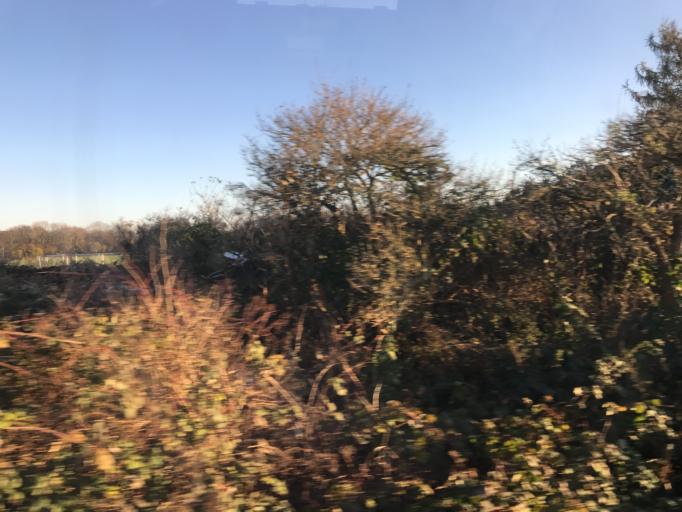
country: DK
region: Capital Region
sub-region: Hvidovre Kommune
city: Hvidovre
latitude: 55.6450
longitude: 12.5059
